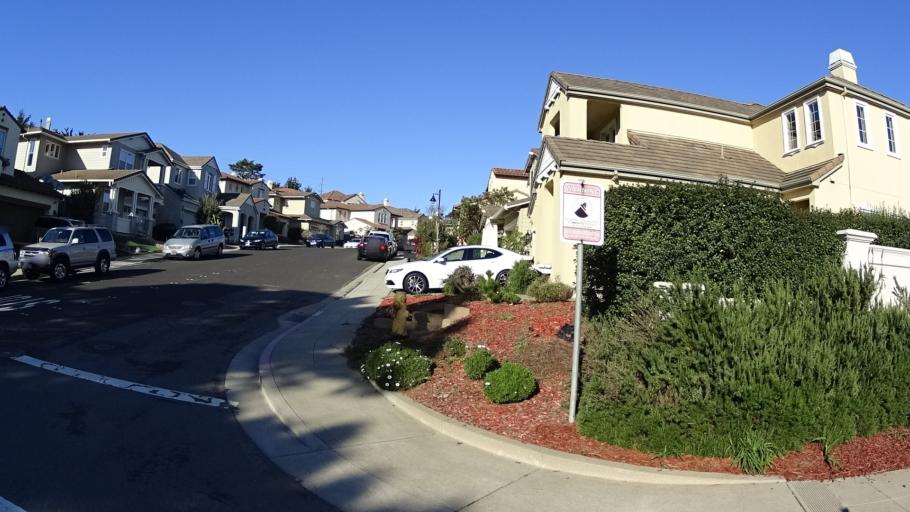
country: US
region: California
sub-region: San Mateo County
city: Pacifica
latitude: 37.6319
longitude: -122.4632
